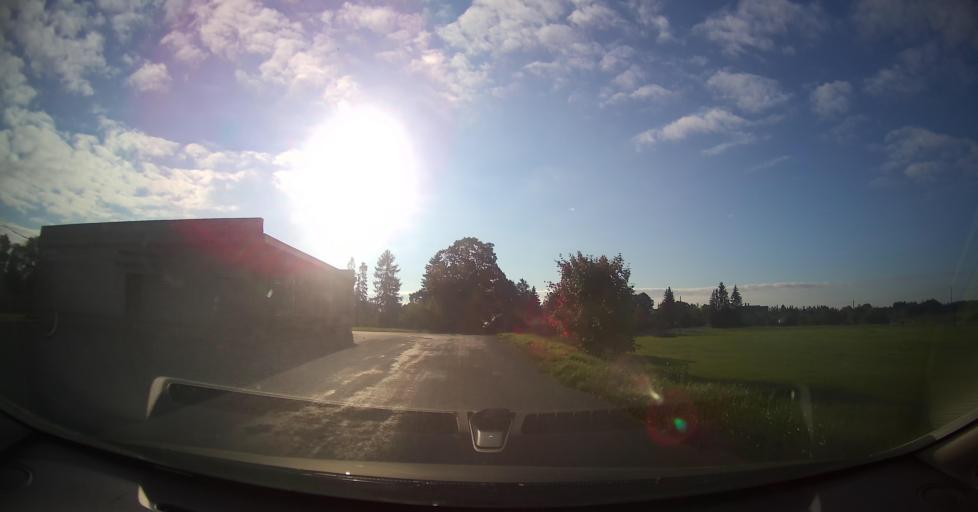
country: EE
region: Harju
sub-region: Joelaehtme vald
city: Loo
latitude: 59.3994
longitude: 24.9328
